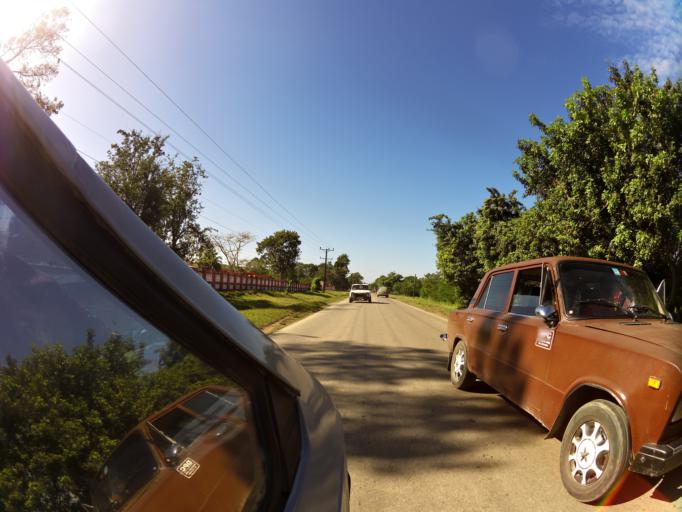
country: CU
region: Las Tunas
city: Las Tunas
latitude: 20.9729
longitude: -76.9100
